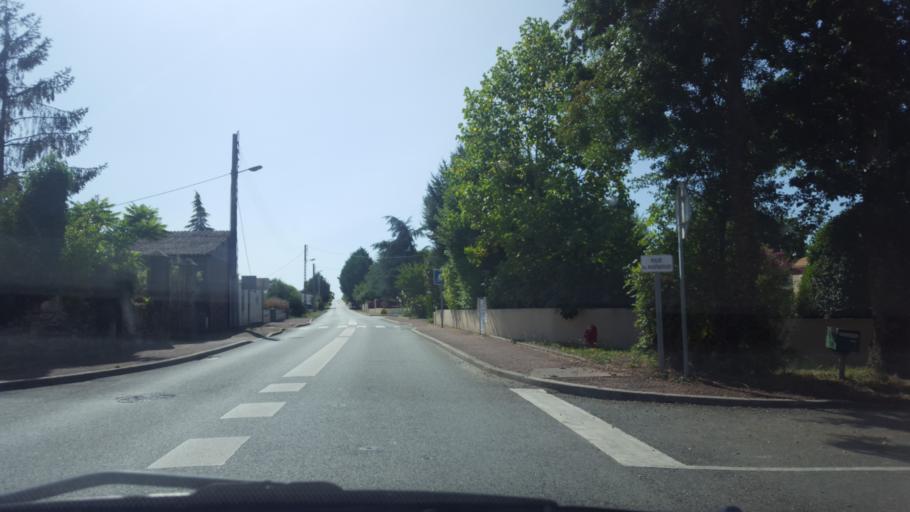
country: FR
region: Pays de la Loire
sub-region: Departement de la Loire-Atlantique
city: La Limouziniere
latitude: 46.9924
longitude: -1.6027
